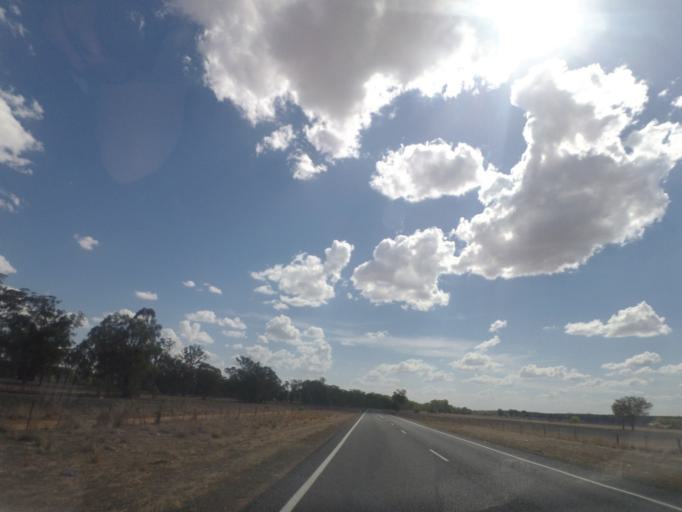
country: AU
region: Queensland
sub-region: Southern Downs
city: Stanthorpe
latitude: -28.3930
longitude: 151.3166
